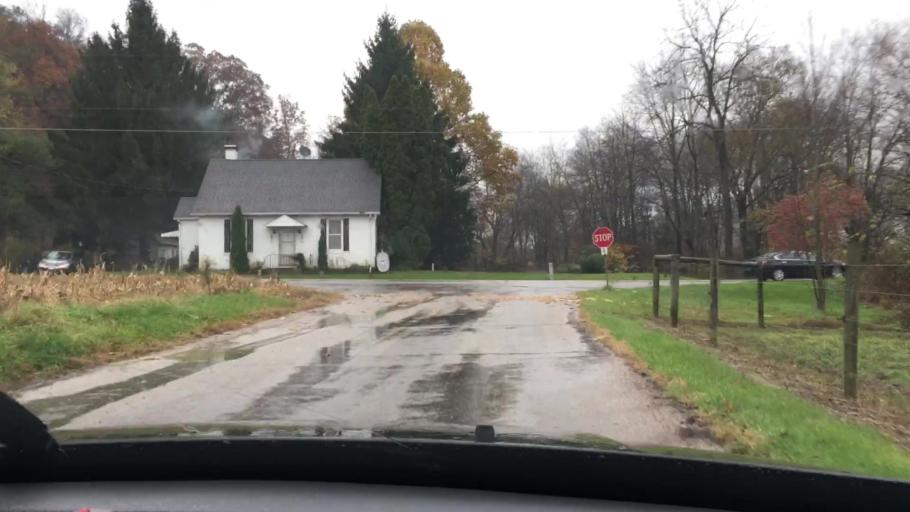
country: US
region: Pennsylvania
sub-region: York County
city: Glen Rock
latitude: 39.7466
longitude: -76.8026
